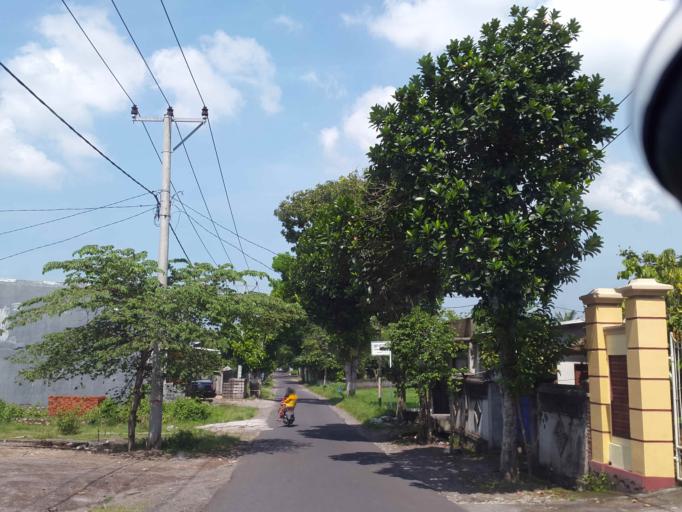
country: ID
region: West Nusa Tenggara
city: Mambalan
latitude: -8.5489
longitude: 116.1229
